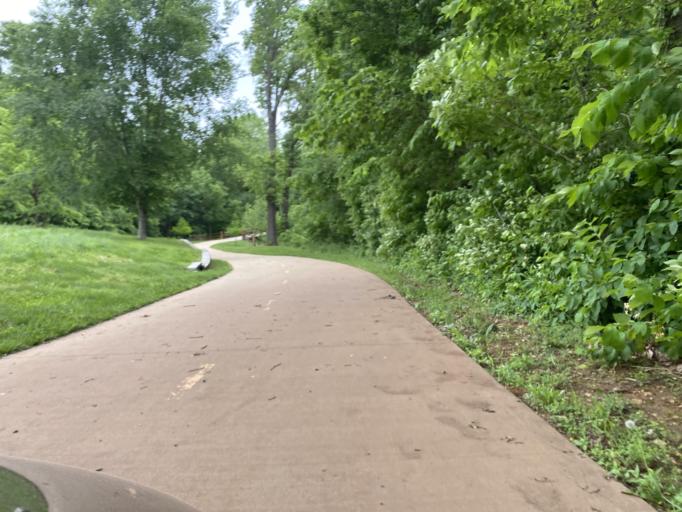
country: US
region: Arkansas
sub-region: Benton County
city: Bentonville
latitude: 36.3681
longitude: -94.2352
